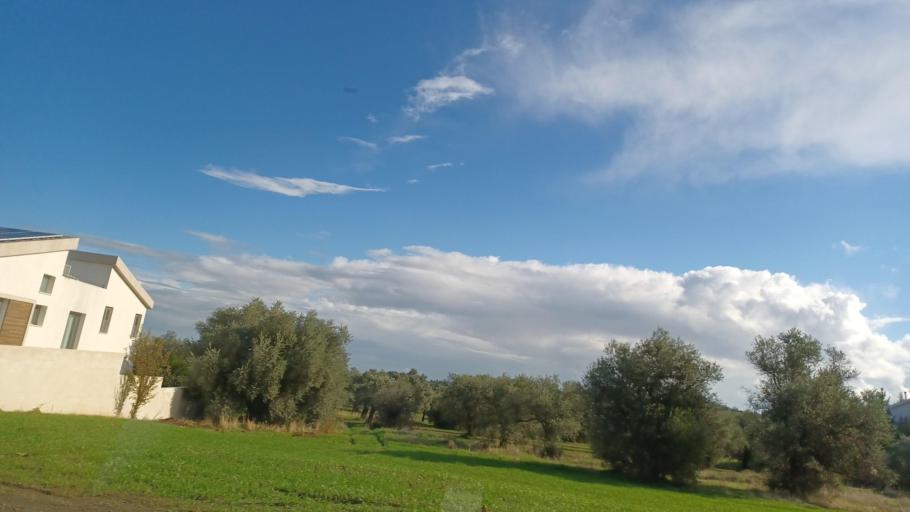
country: CY
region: Lefkosia
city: Lythrodontas
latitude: 34.9414
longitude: 33.2965
